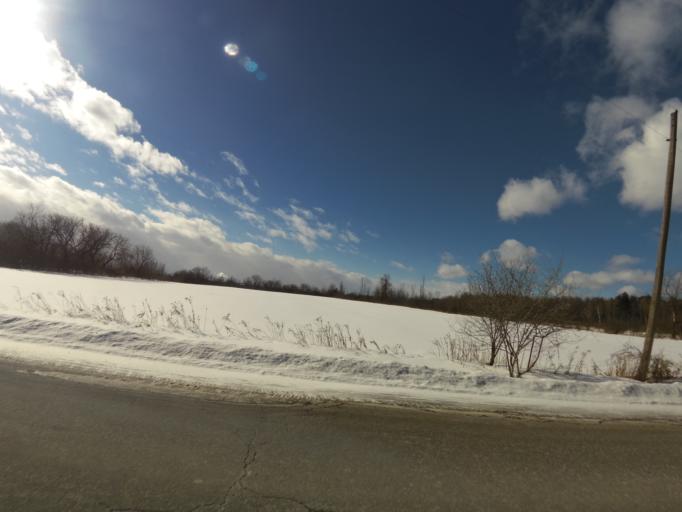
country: CA
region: Ontario
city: Ottawa
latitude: 45.3914
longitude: -75.5794
